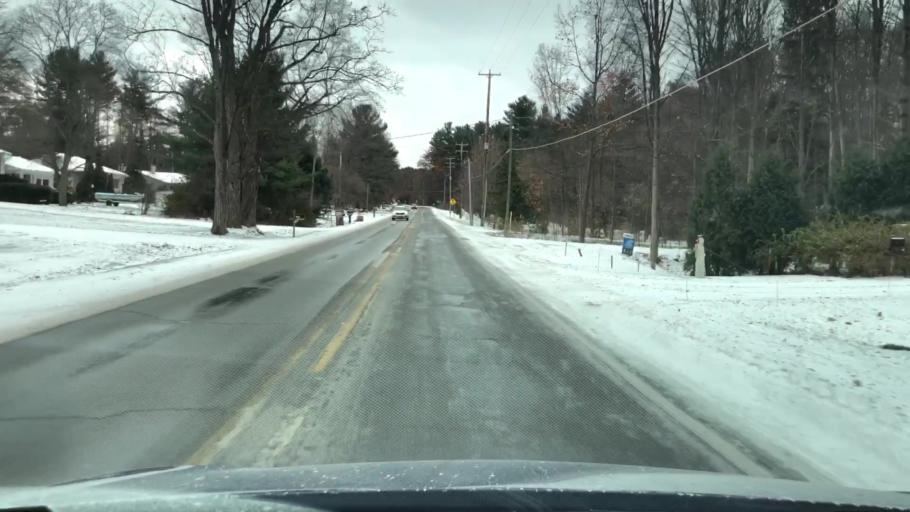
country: US
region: Michigan
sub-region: Grand Traverse County
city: Traverse City
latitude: 44.7770
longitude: -85.5909
